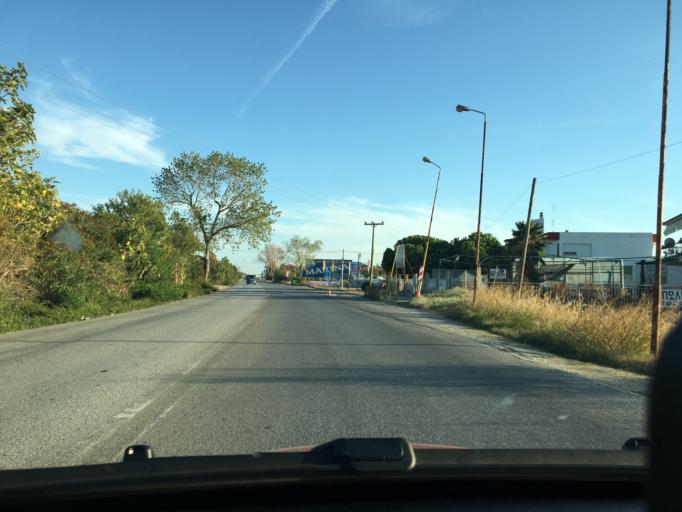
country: GR
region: Central Macedonia
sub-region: Nomos Chalkidikis
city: Nea Potidhaia
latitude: 40.2038
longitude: 23.3247
